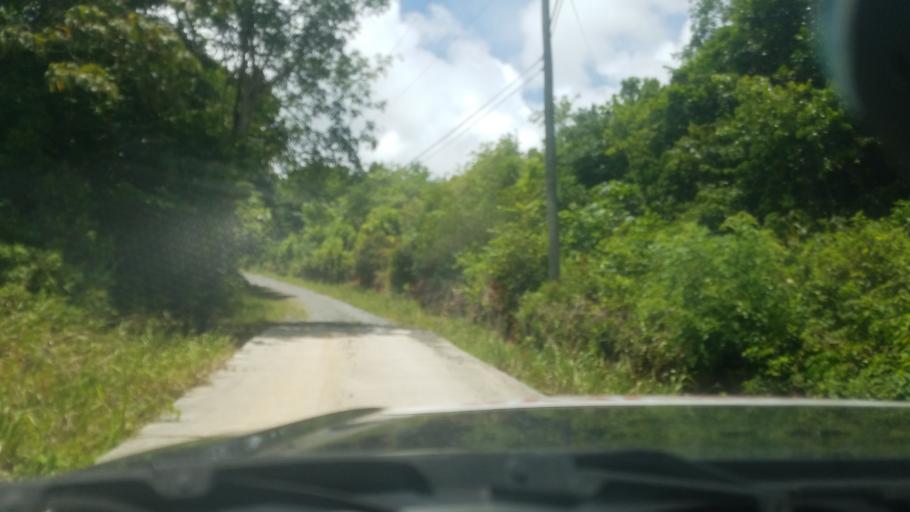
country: LC
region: Praslin
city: Praslin
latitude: 13.8666
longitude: -60.9096
